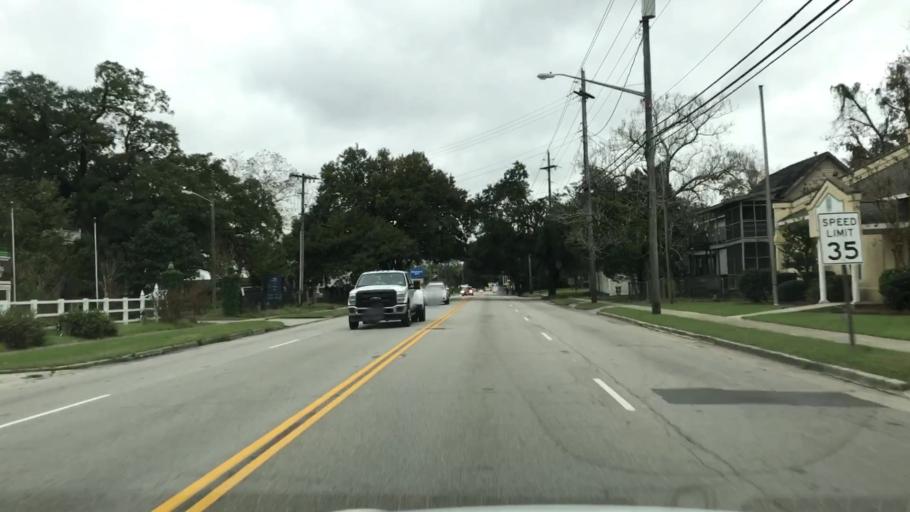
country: US
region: South Carolina
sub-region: Georgetown County
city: Georgetown
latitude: 33.3706
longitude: -79.2787
